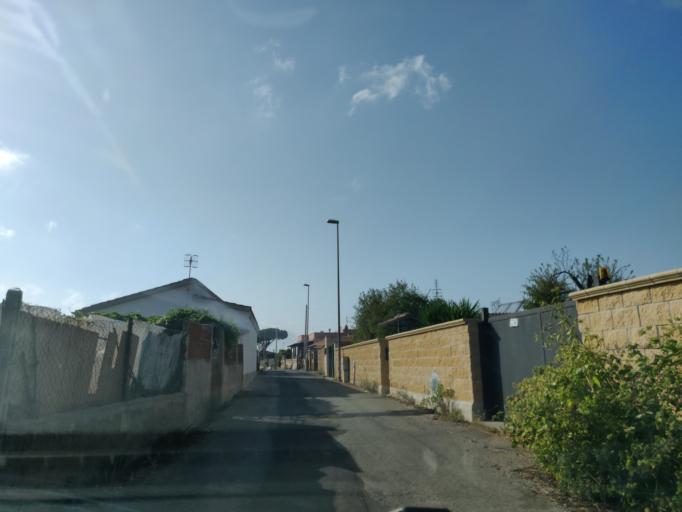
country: IT
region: Latium
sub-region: Citta metropolitana di Roma Capitale
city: Aurelia
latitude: 42.1271
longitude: 11.7705
